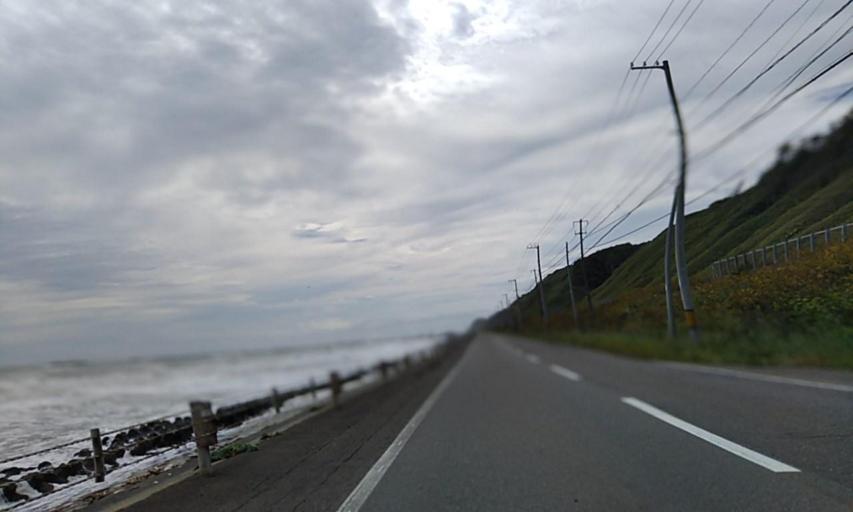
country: JP
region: Hokkaido
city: Kushiro
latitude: 42.8152
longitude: 143.8309
